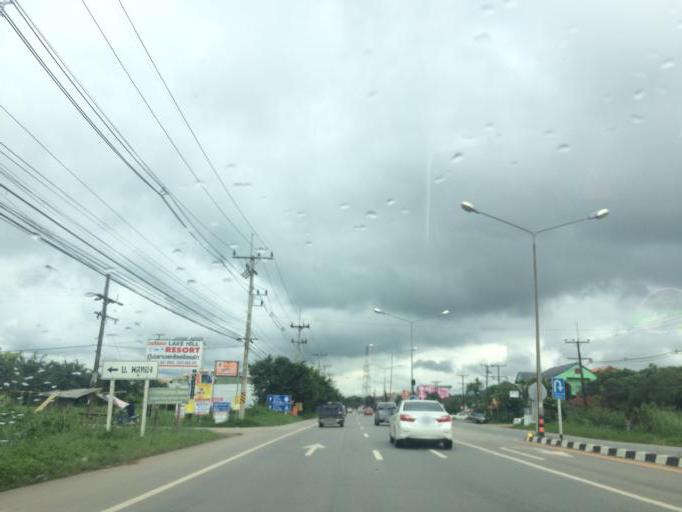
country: TH
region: Chiang Rai
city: Mae Chan
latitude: 20.0396
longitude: 99.8757
